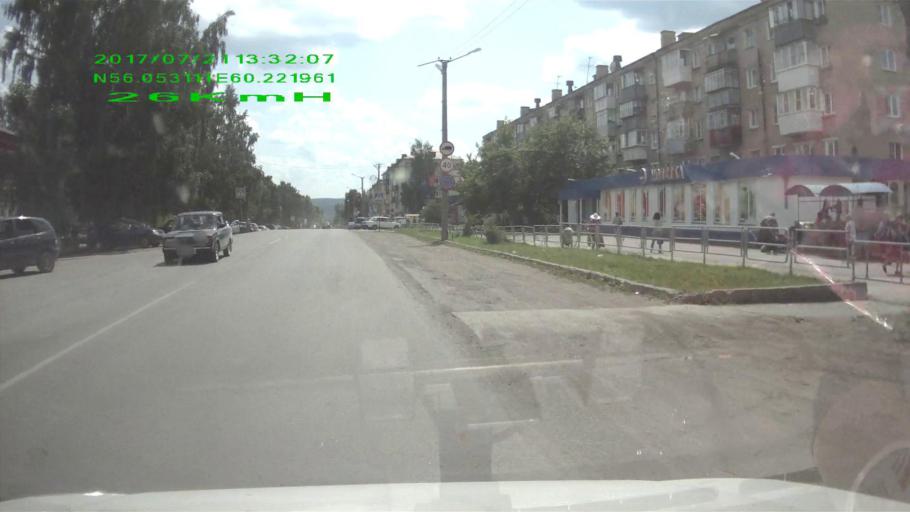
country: RU
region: Chelyabinsk
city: Verkhniy Ufaley
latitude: 56.0527
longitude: 60.2221
